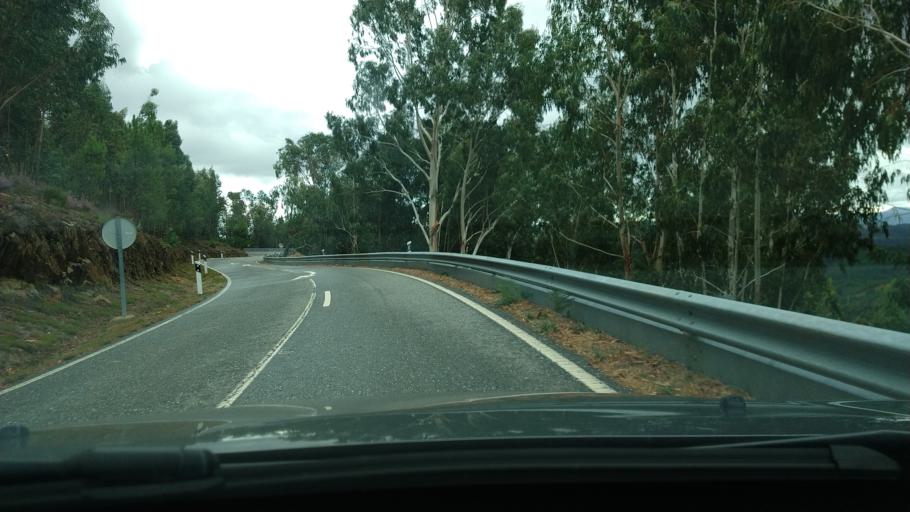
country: PT
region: Castelo Branco
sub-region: Covilha
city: Covilha
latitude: 40.2395
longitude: -7.6563
